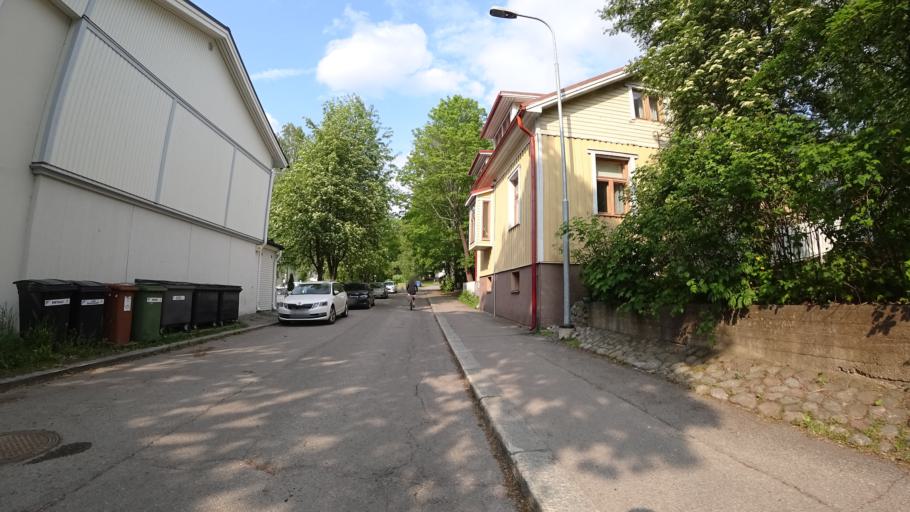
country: FI
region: Pirkanmaa
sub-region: Tampere
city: Tampere
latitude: 61.4979
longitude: 23.7145
